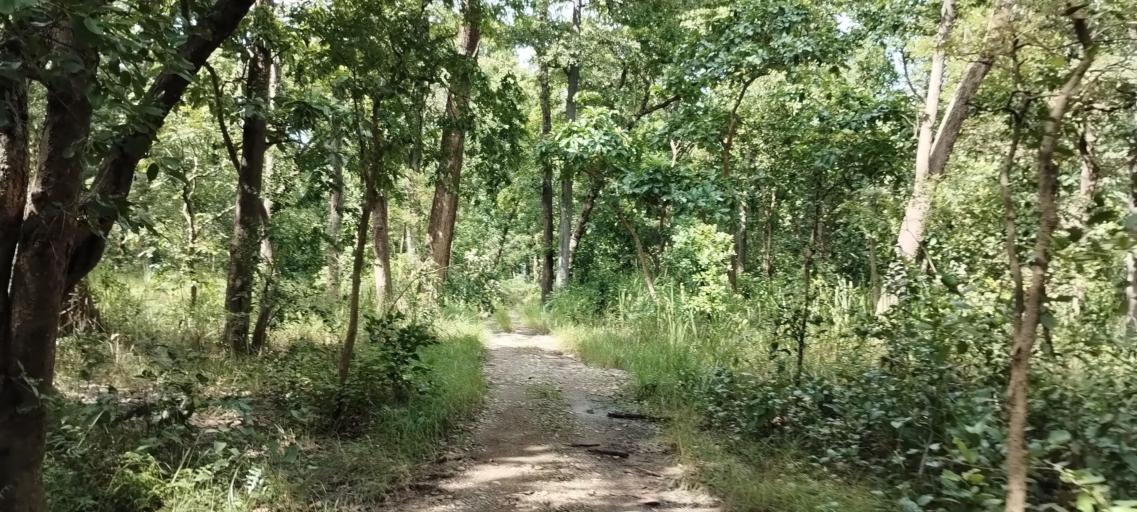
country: NP
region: Far Western
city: Tikapur
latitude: 28.5407
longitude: 81.2865
